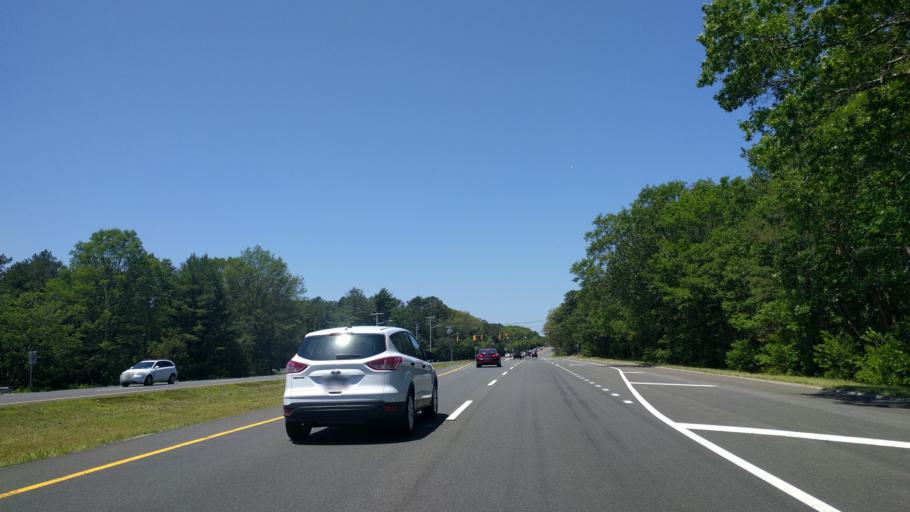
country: US
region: New York
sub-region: Suffolk County
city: Manorville
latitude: 40.8640
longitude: -72.7774
